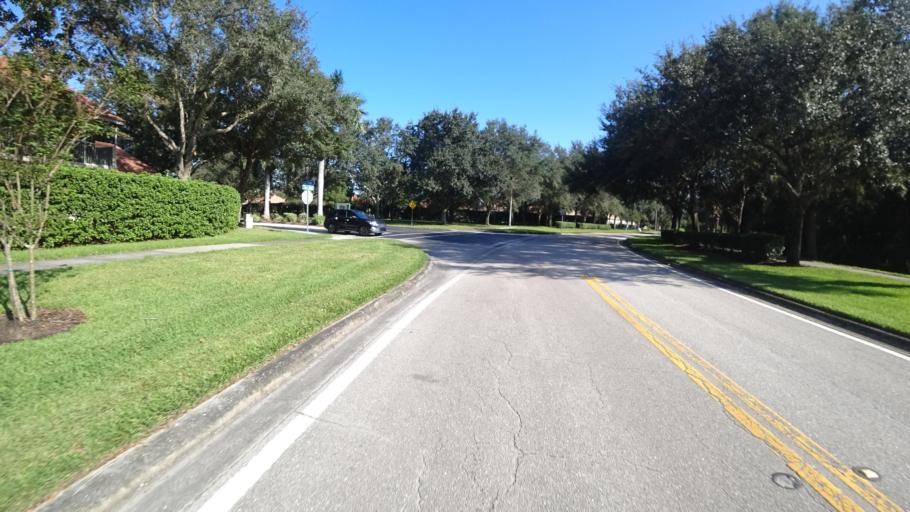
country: US
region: Florida
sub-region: Sarasota County
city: Desoto Lakes
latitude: 27.4224
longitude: -82.4653
